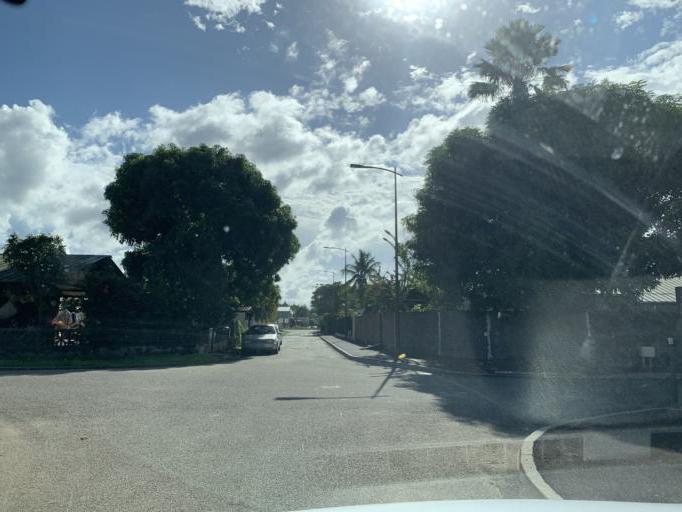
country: GF
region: Guyane
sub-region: Guyane
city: Kourou
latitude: 5.1735
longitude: -52.6460
